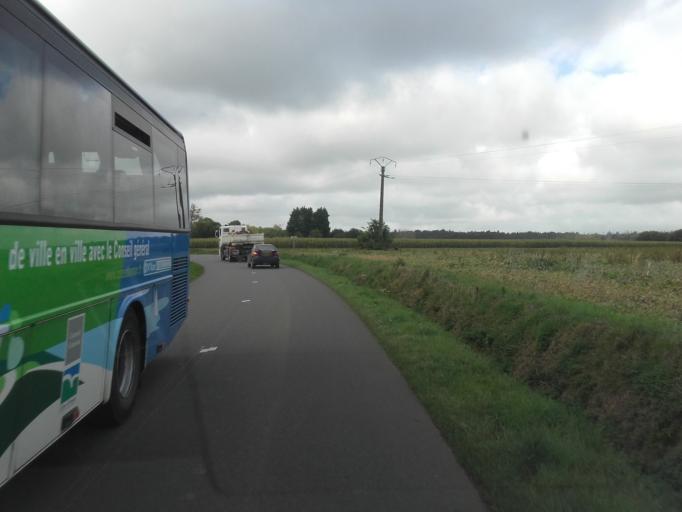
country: FR
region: Brittany
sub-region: Departement des Cotes-d'Armor
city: Plelo
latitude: 48.5729
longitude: -2.9502
